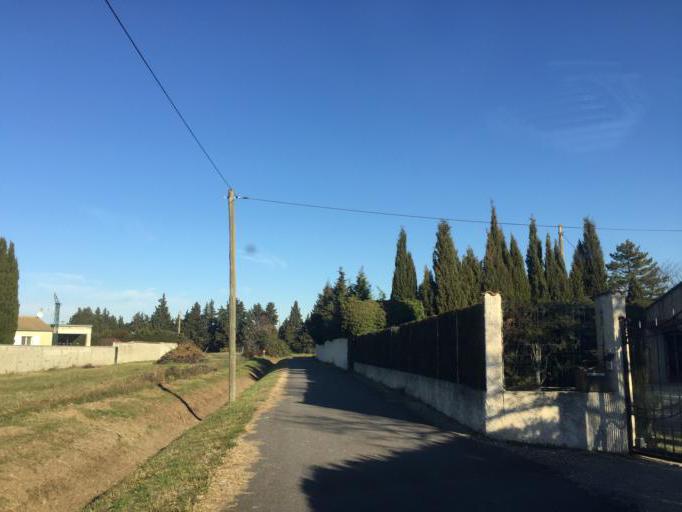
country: FR
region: Provence-Alpes-Cote d'Azur
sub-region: Departement du Vaucluse
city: Orange
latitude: 44.1495
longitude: 4.8151
